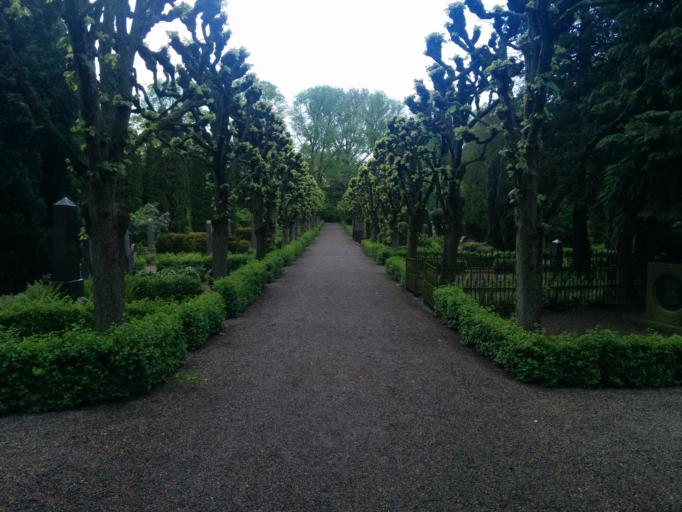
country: SE
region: Skane
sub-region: Lunds Kommun
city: Lund
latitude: 55.7016
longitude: 13.2012
